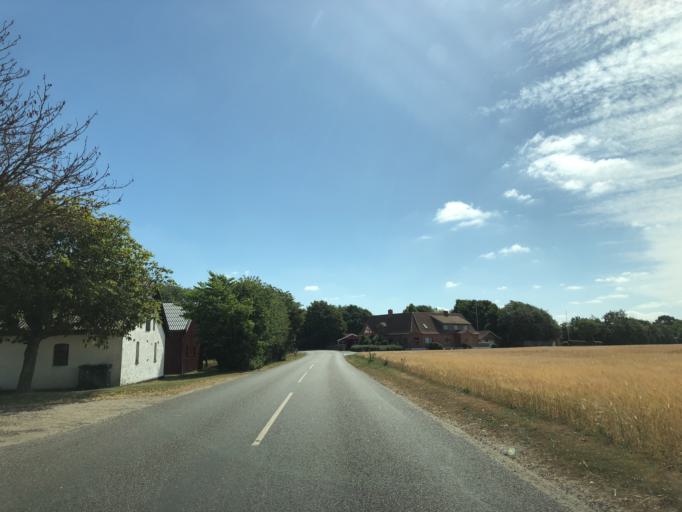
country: DK
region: North Denmark
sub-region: Vesthimmerland Kommune
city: Alestrup
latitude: 56.5748
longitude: 9.5400
